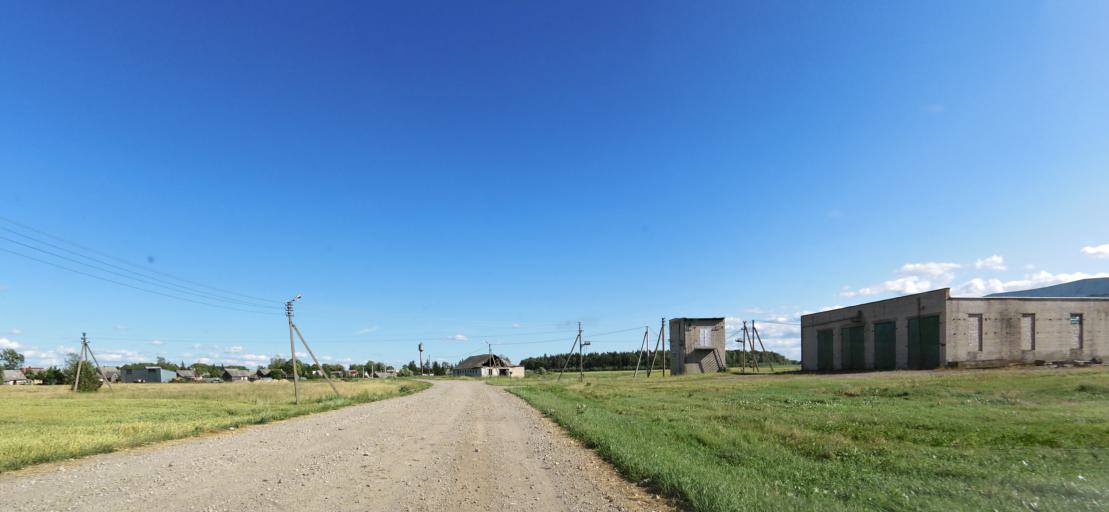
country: LT
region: Panevezys
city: Pasvalys
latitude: 56.1607
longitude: 24.4347
